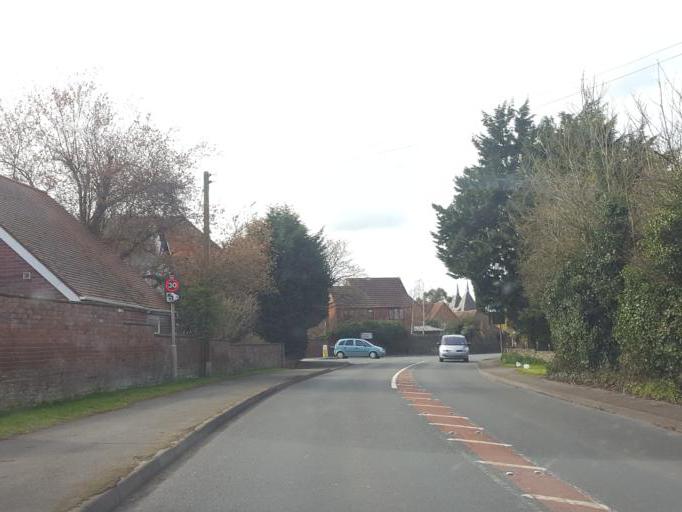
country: GB
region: England
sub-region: Worcestershire
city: Leigh
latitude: 52.1549
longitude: -2.3187
